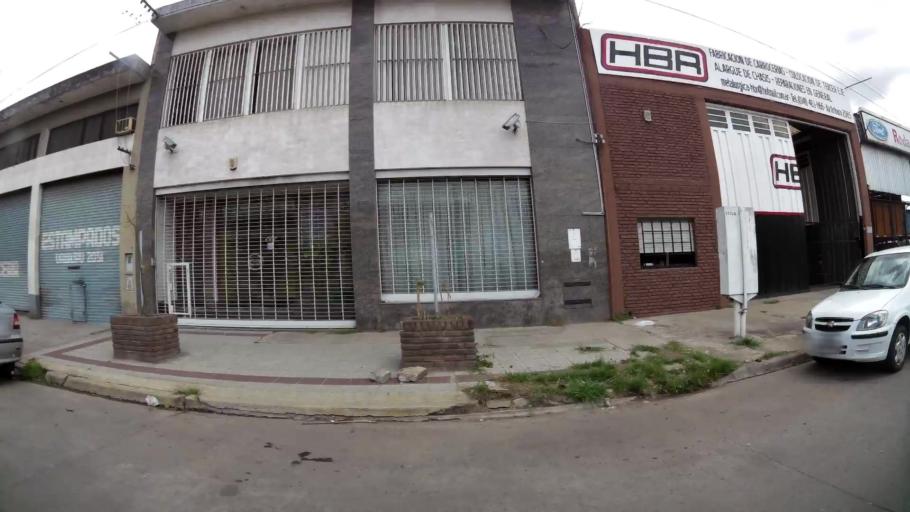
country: AR
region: Santa Fe
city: Gobernador Galvez
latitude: -32.9913
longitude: -60.6639
